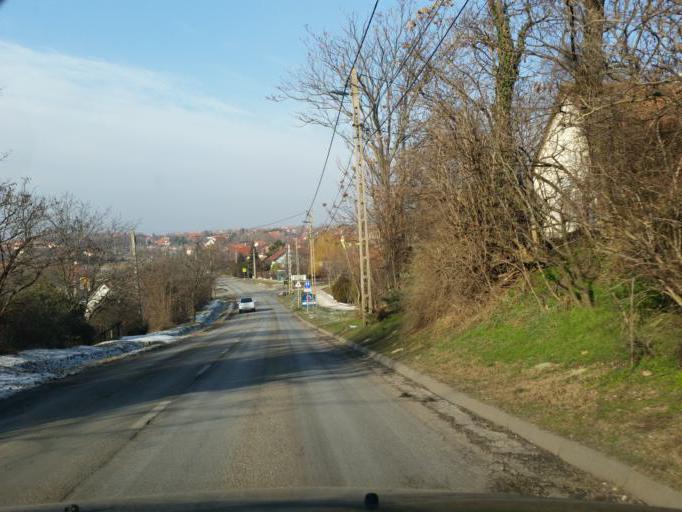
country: HU
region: Pest
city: Telki
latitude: 47.5478
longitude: 18.8262
